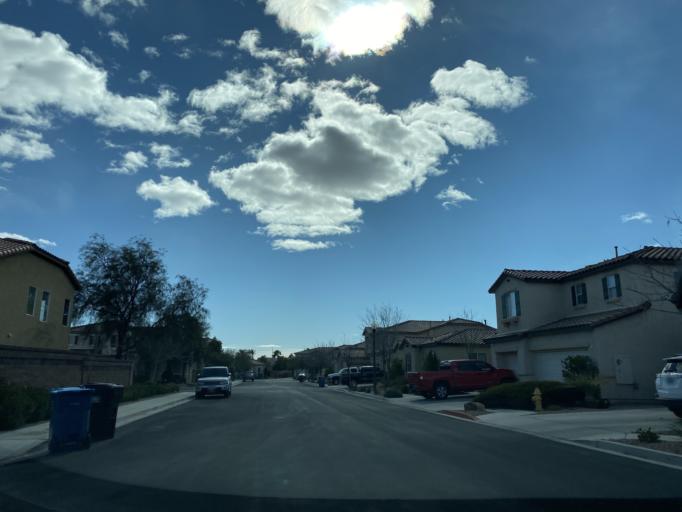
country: US
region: Nevada
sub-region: Clark County
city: Summerlin South
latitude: 36.2972
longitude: -115.3032
